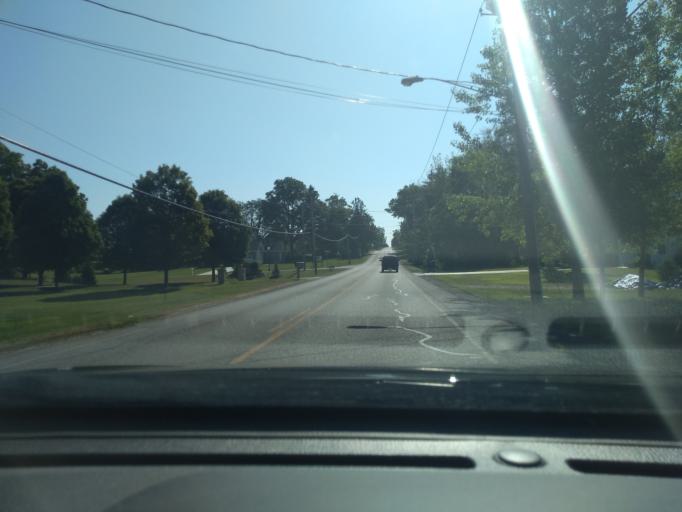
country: US
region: New York
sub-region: Erie County
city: Orchard Park
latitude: 42.7894
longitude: -78.7075
